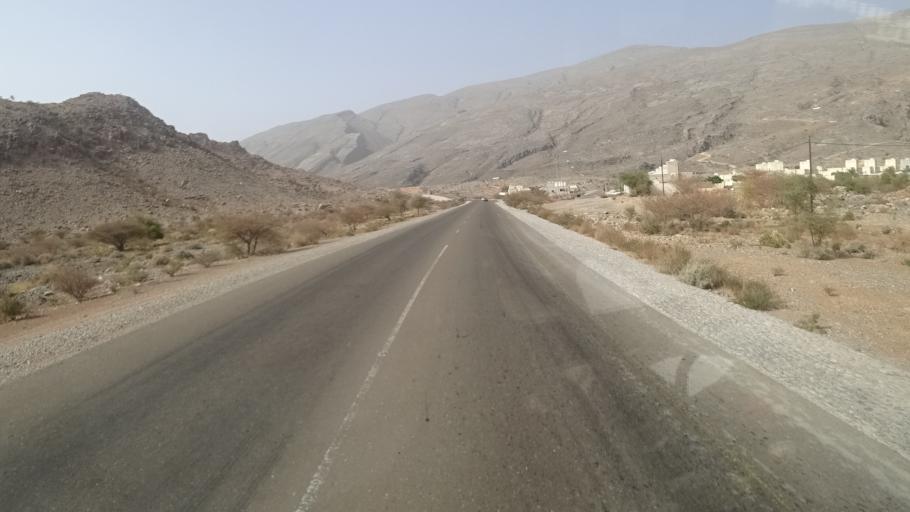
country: OM
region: Muhafazat ad Dakhiliyah
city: Nizwa
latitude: 22.9926
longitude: 57.5835
